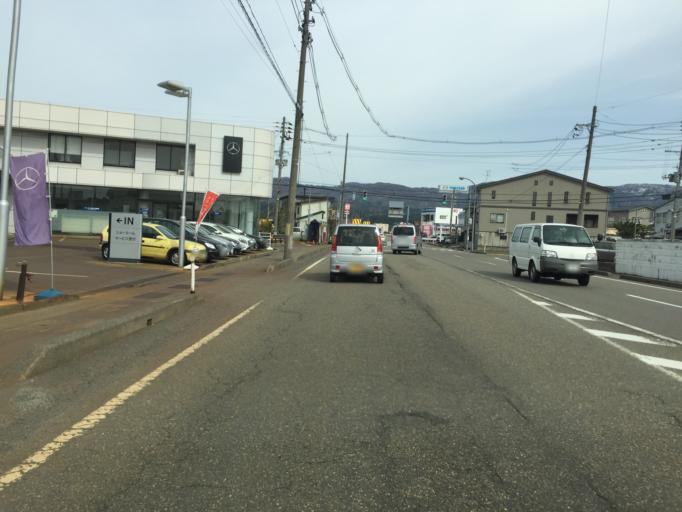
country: JP
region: Niigata
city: Nagaoka
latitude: 37.4563
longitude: 138.8798
